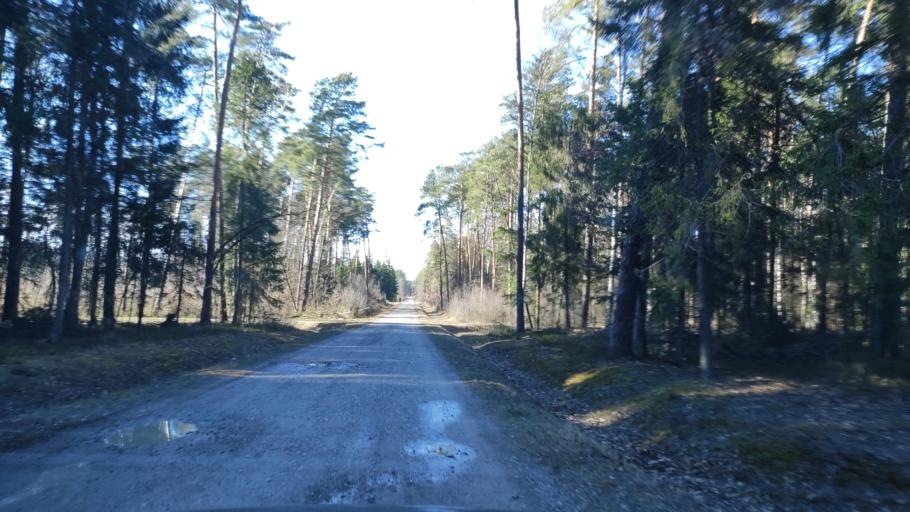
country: PL
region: Masovian Voivodeship
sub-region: Powiat radomski
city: Jedlnia-Letnisko
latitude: 51.4694
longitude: 21.3071
